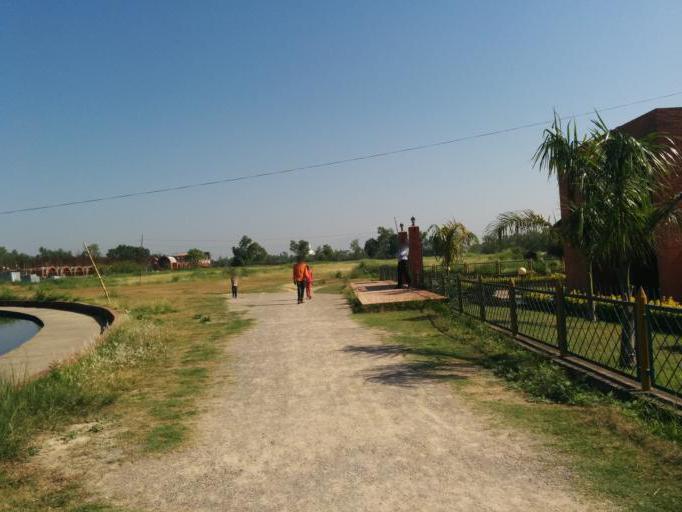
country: IN
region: Uttar Pradesh
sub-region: Maharajganj
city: Nautanwa
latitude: 27.4892
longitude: 83.2766
